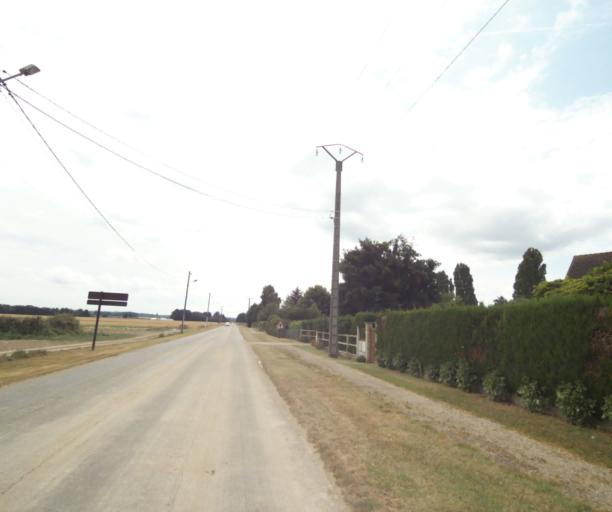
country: FR
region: Ile-de-France
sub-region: Departement de Seine-et-Marne
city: Arbonne-la-Foret
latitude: 48.4284
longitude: 2.5818
